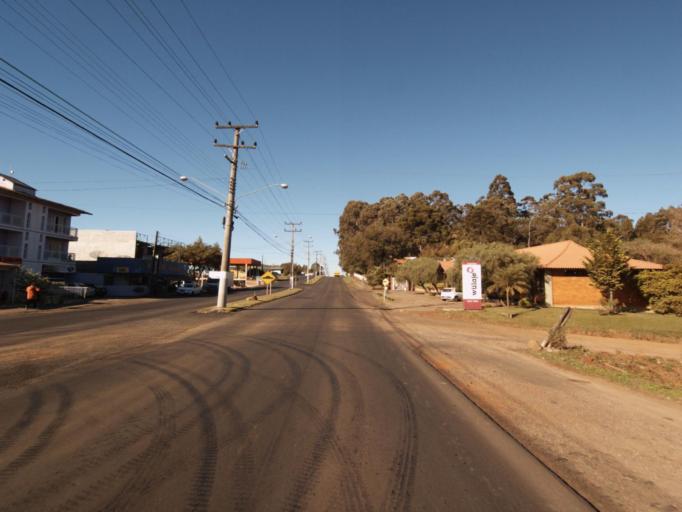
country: AR
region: Misiones
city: Bernardo de Irigoyen
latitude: -26.7508
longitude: -53.5009
